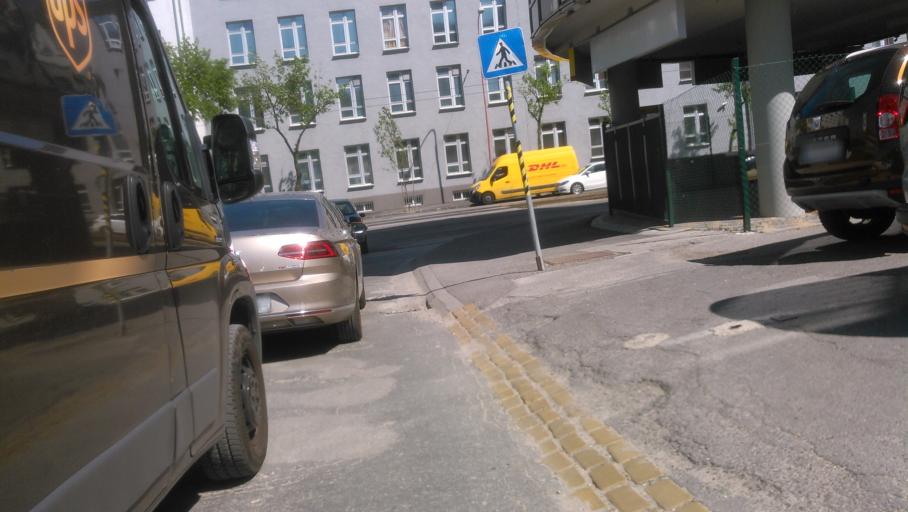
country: SK
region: Bratislavsky
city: Bratislava
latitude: 48.1725
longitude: 17.1266
